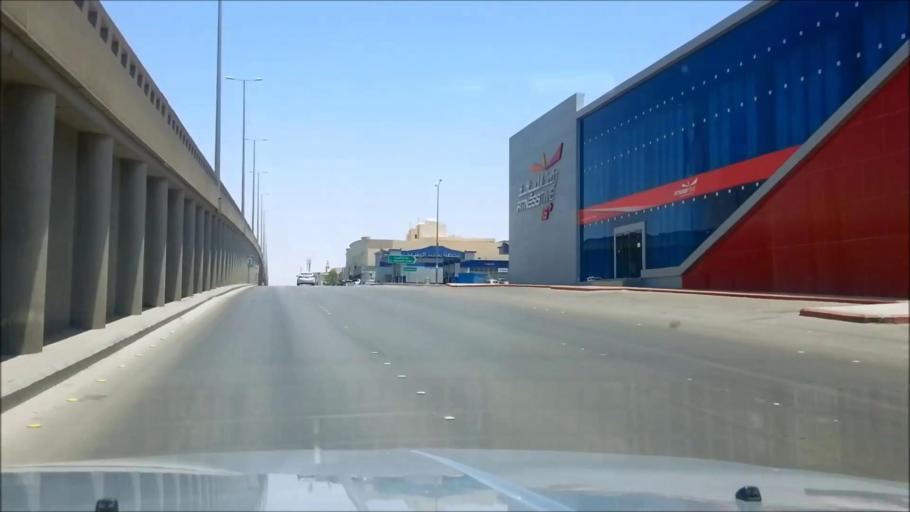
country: SA
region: Ar Riyad
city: Riyadh
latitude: 24.7712
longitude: 46.6679
